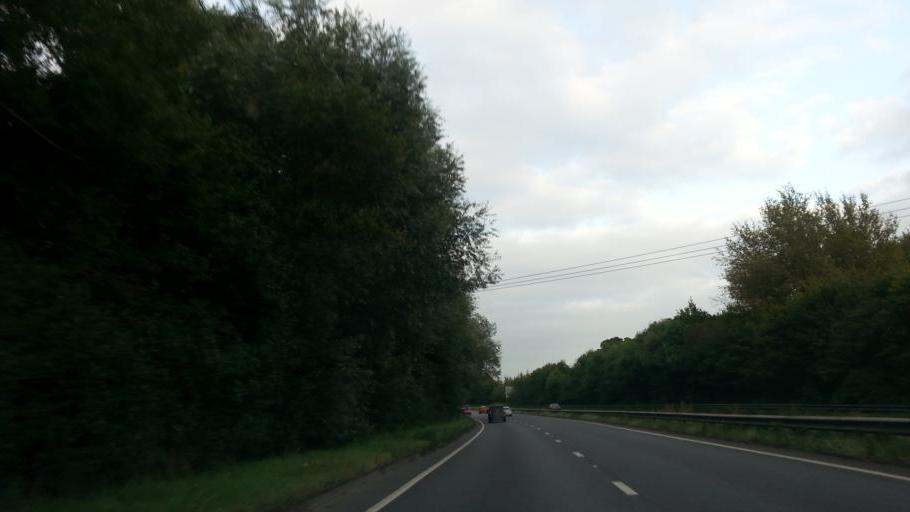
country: GB
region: England
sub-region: Northamptonshire
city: Brackley
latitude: 52.0212
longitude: -1.1466
